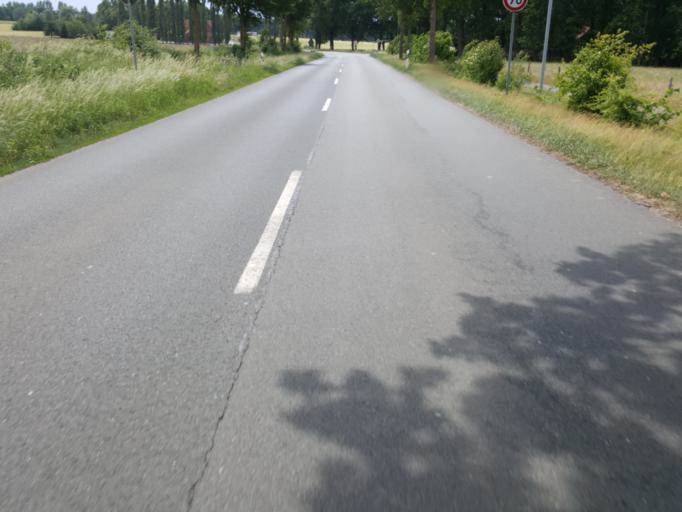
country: DE
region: Lower Saxony
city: Husum
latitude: 52.5755
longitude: 9.2479
